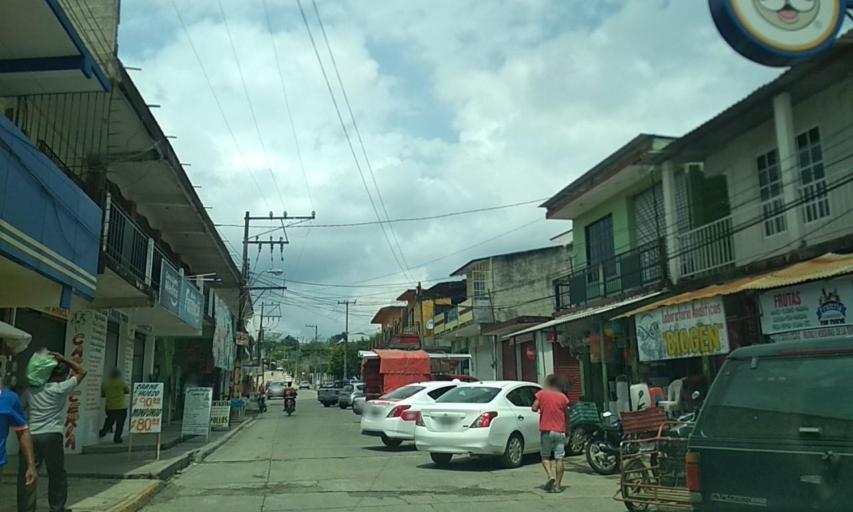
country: MX
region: Veracruz
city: Las Choapas
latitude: 17.8938
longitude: -94.1046
